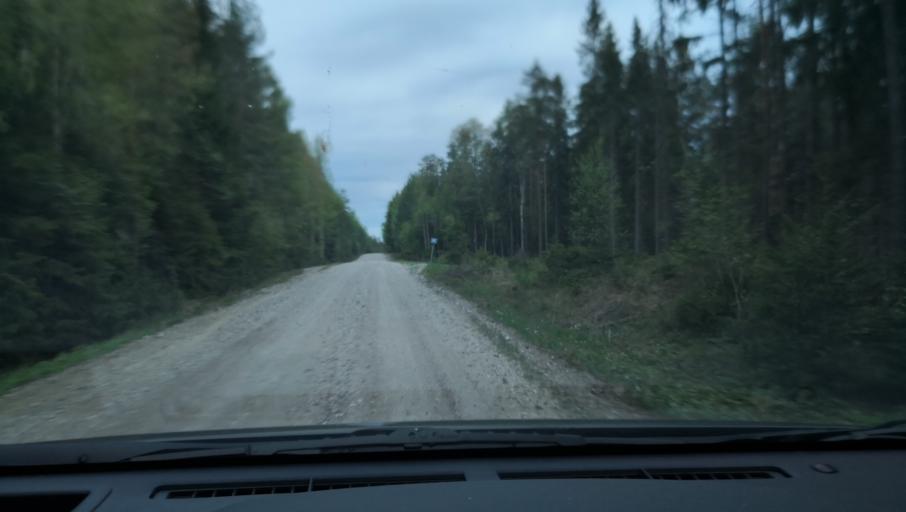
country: SE
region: Vaestmanland
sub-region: Skinnskattebergs Kommun
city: Skinnskatteberg
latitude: 59.7673
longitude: 15.4564
